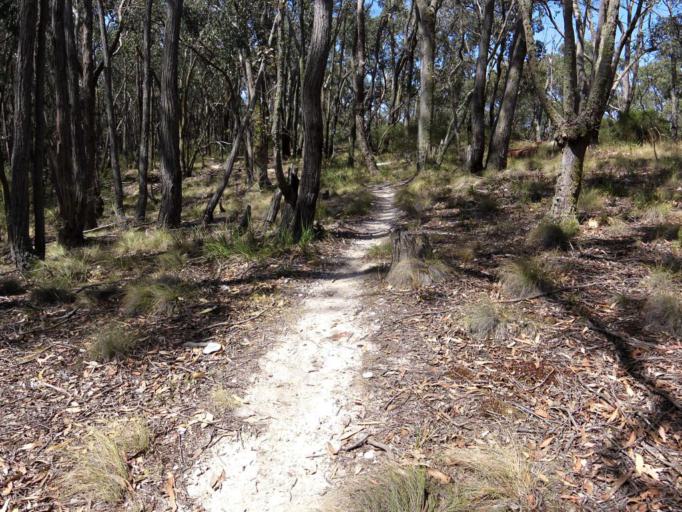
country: AU
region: Victoria
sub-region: Melton
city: Melton West
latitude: -37.5153
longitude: 144.5552
